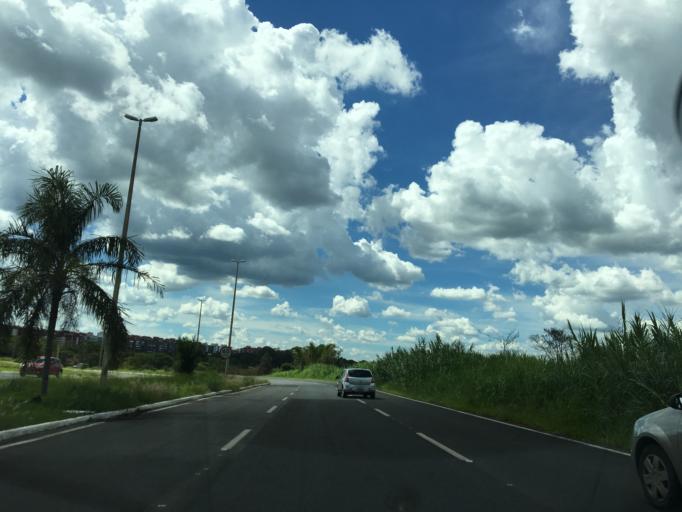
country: BR
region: Federal District
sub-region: Brasilia
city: Brasilia
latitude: -15.7473
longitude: -47.8802
